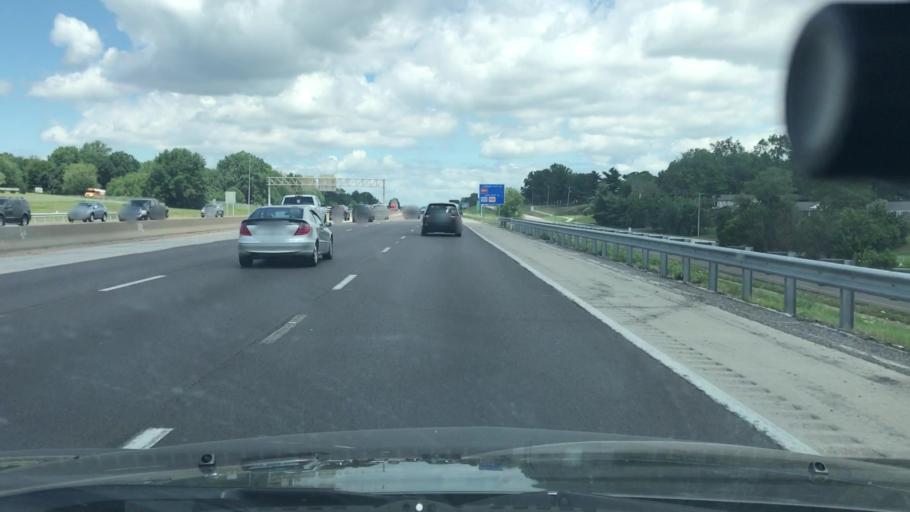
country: US
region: Missouri
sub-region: Saint Louis County
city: Creve Coeur
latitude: 38.6561
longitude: -90.4480
